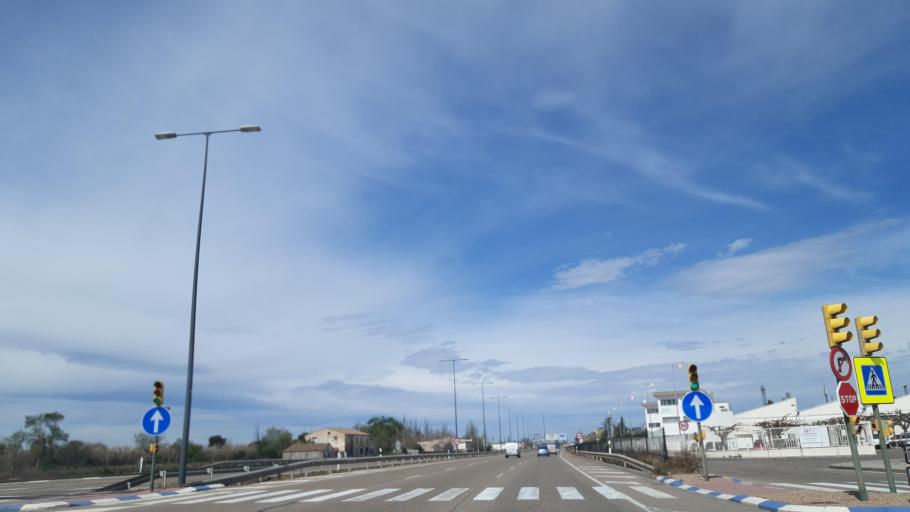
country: ES
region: Aragon
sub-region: Provincia de Zaragoza
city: Utebo
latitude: 41.6857
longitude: -0.9713
